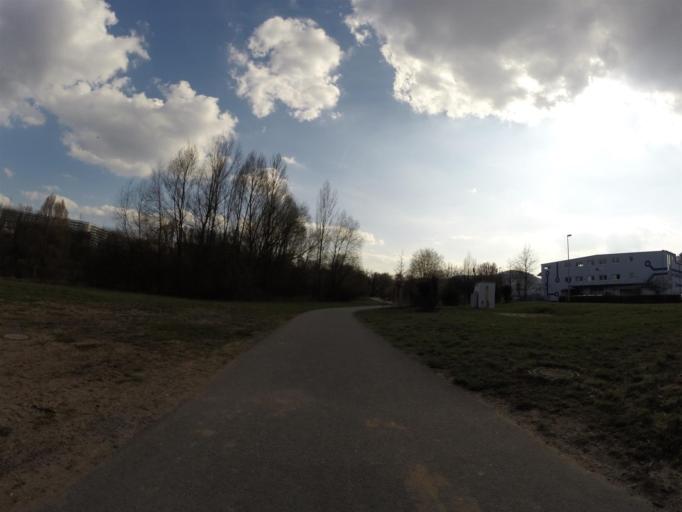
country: DE
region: Thuringia
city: Sulza
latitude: 50.8853
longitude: 11.6013
